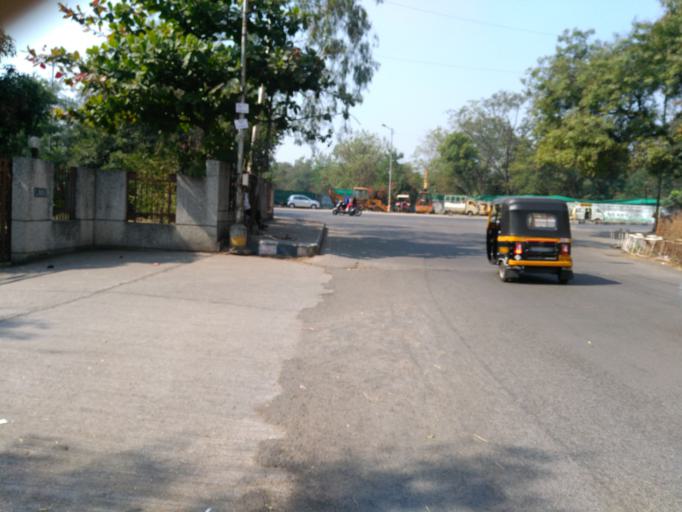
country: IN
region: Maharashtra
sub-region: Pune Division
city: Khadki
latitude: 18.5548
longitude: 73.8907
